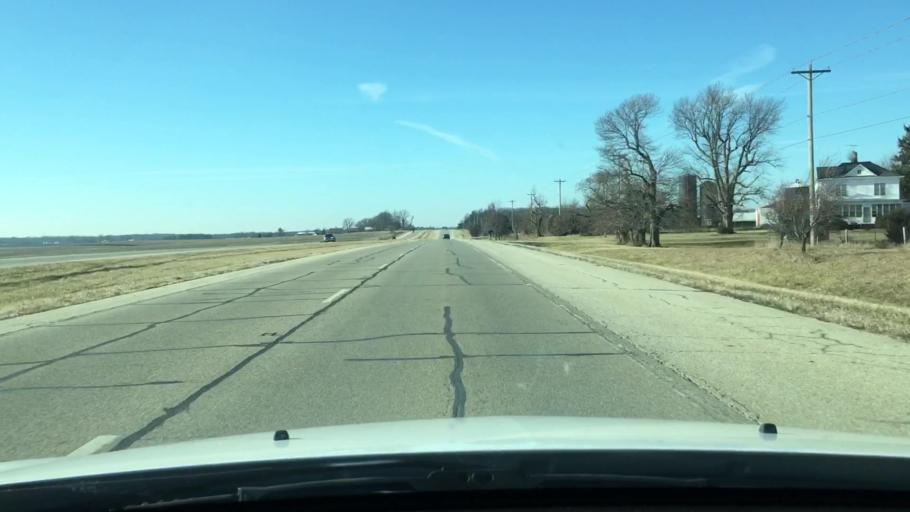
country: US
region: Illinois
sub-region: Woodford County
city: Metamora
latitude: 40.7817
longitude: -89.3997
